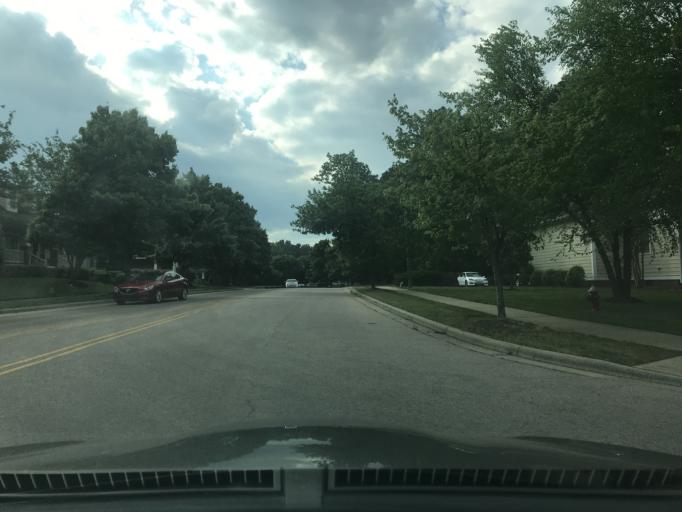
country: US
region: North Carolina
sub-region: Wake County
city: Wake Forest
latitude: 35.9172
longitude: -78.5682
